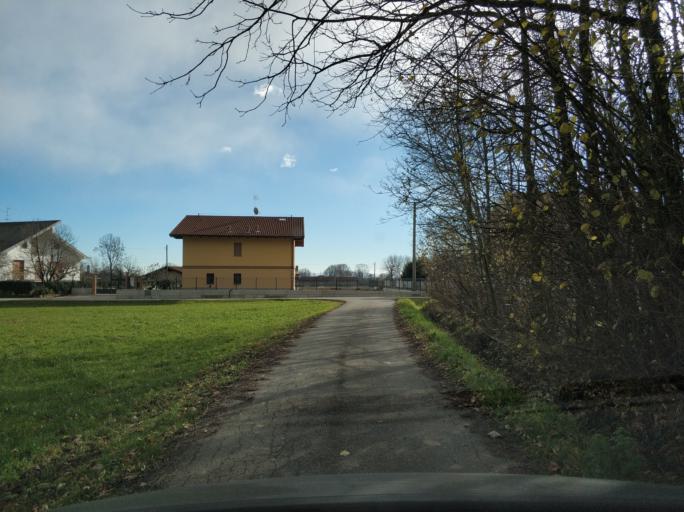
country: IT
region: Piedmont
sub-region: Provincia di Torino
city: Robassomero
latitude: 45.2156
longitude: 7.5797
